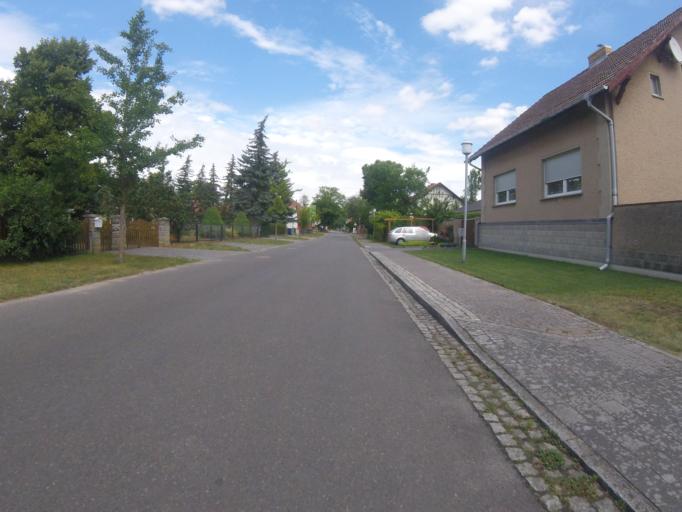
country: DE
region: Brandenburg
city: Bestensee
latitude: 52.2378
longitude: 13.7078
